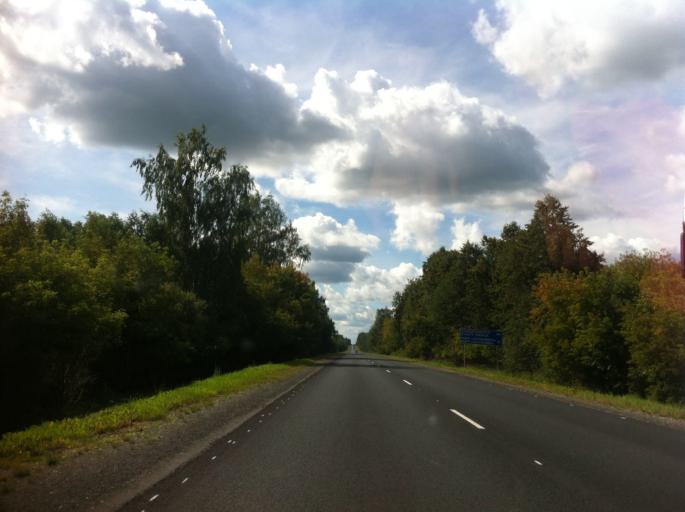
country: RU
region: Pskov
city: Izborsk
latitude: 57.7249
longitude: 27.9510
